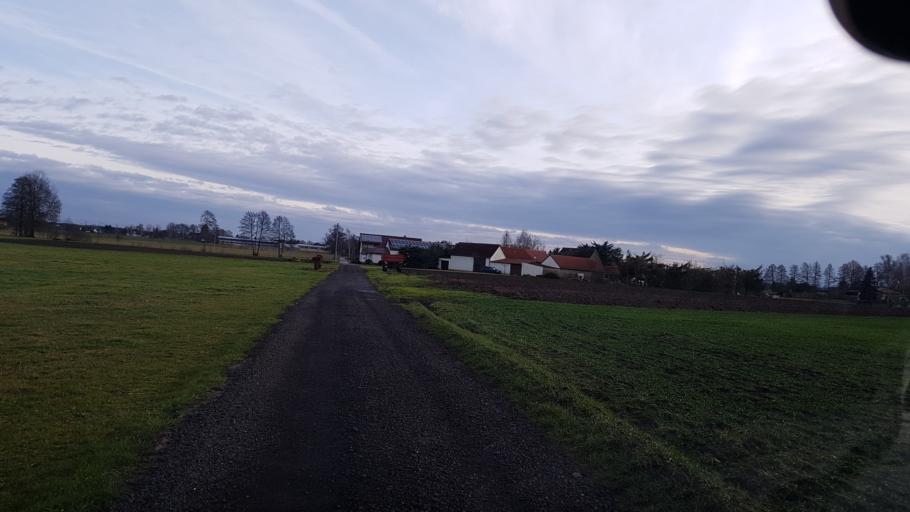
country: DE
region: Brandenburg
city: Sallgast
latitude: 51.6446
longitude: 13.8477
